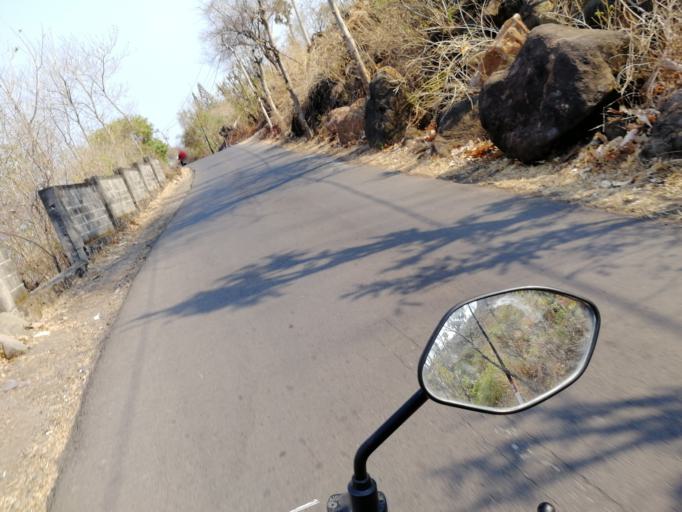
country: ID
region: Bali
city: Biaslantang Kaler
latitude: -8.3625
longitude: 115.6989
